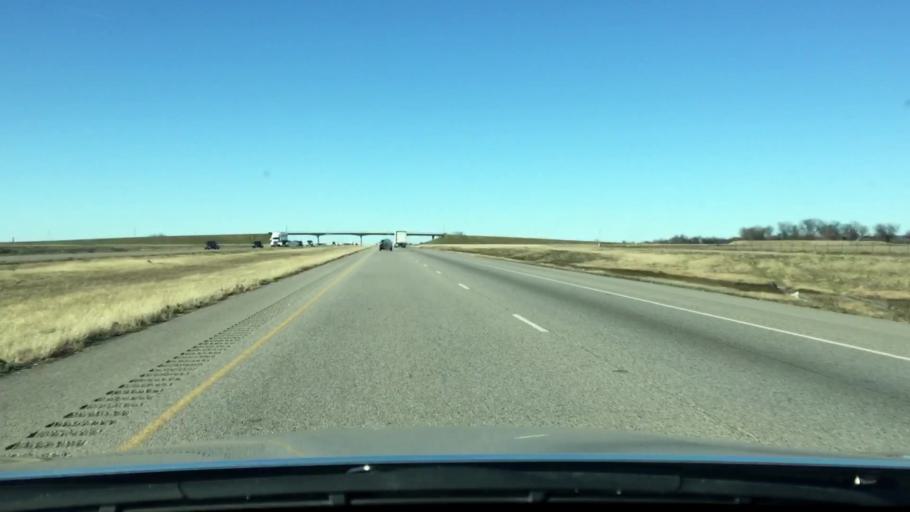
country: US
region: Texas
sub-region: Hill County
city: Itasca
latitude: 32.1219
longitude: -97.1166
